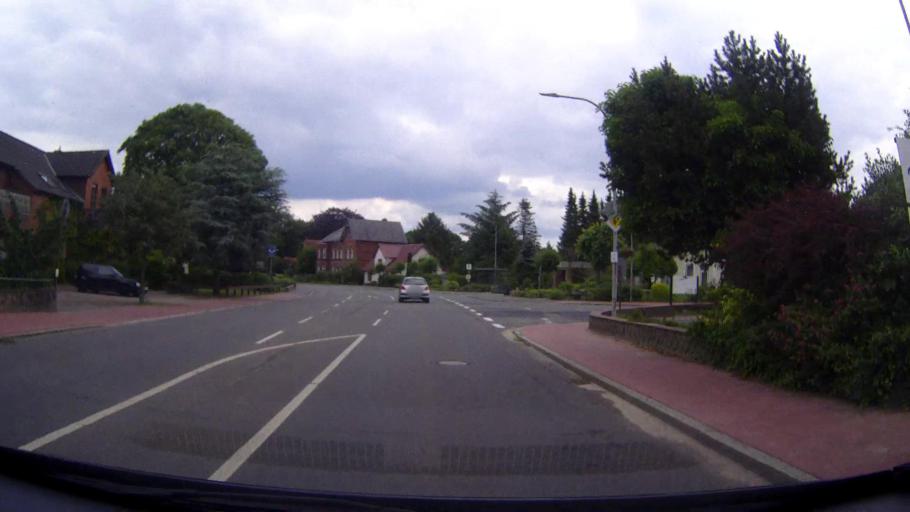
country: DE
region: Schleswig-Holstein
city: Hanerau-Hademarschen
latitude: 54.1214
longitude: 9.4285
